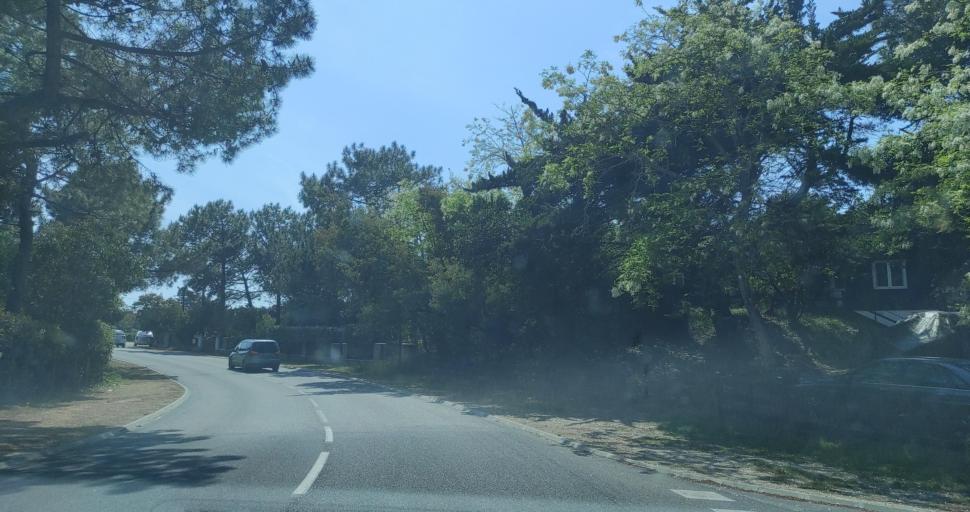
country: FR
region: Aquitaine
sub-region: Departement de la Gironde
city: Arcachon
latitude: 44.6483
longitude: -1.2533
